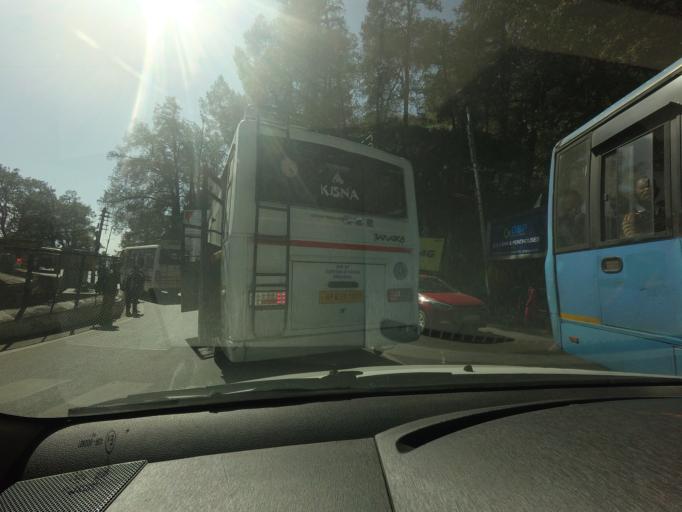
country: IN
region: Himachal Pradesh
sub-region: Shimla
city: Shimla
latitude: 31.1026
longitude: 77.1526
